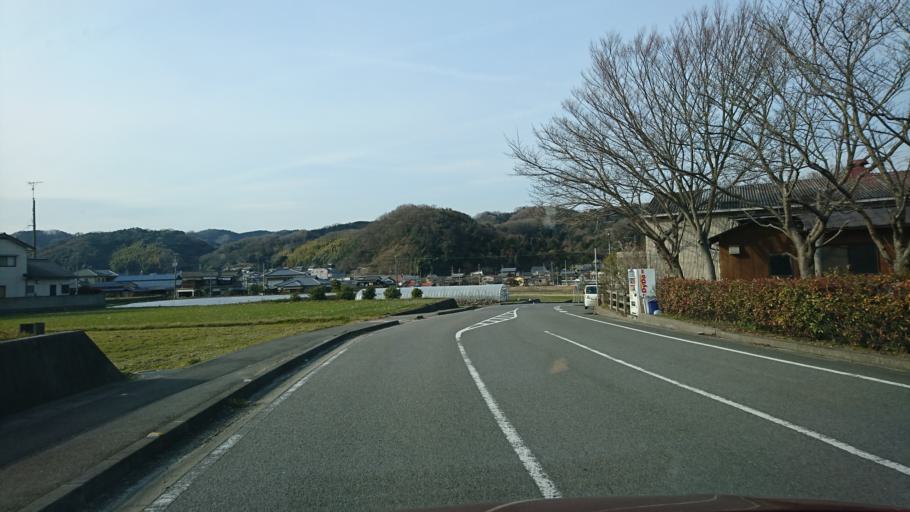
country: JP
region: Ehime
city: Hojo
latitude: 34.0247
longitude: 132.9609
